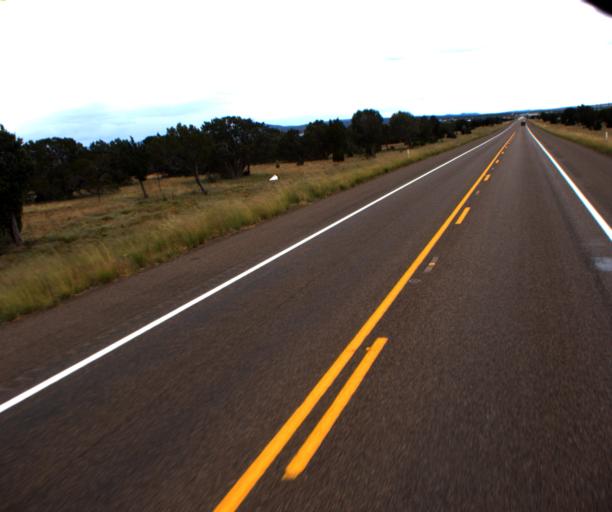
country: US
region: Arizona
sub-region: Navajo County
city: Show Low
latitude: 34.2854
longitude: -110.0291
